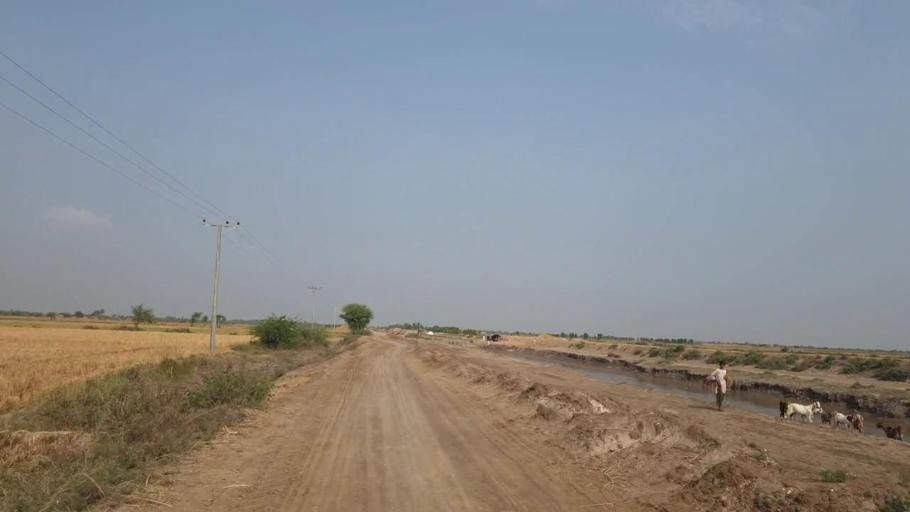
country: PK
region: Sindh
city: Badin
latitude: 24.7401
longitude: 68.7649
